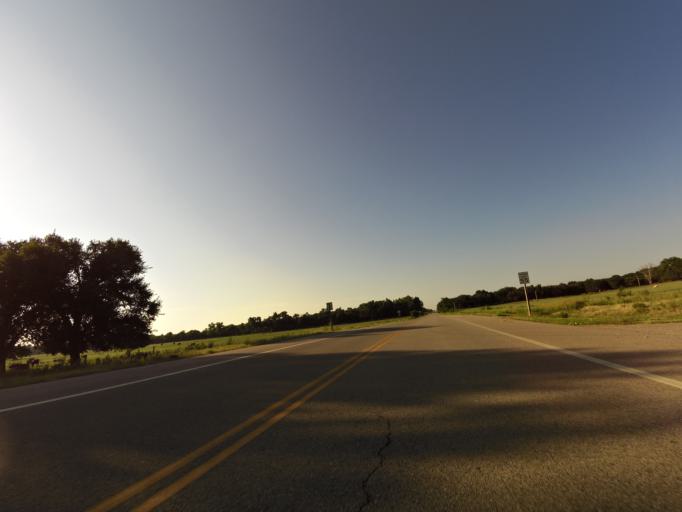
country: US
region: Kansas
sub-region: Reno County
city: Buhler
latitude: 38.1553
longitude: -97.8487
